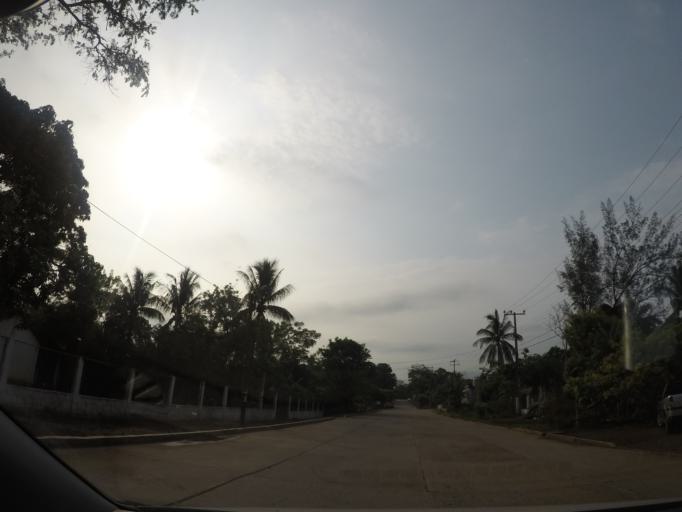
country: MX
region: Oaxaca
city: Colonia Rincon Viejo
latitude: 16.8853
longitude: -95.0473
